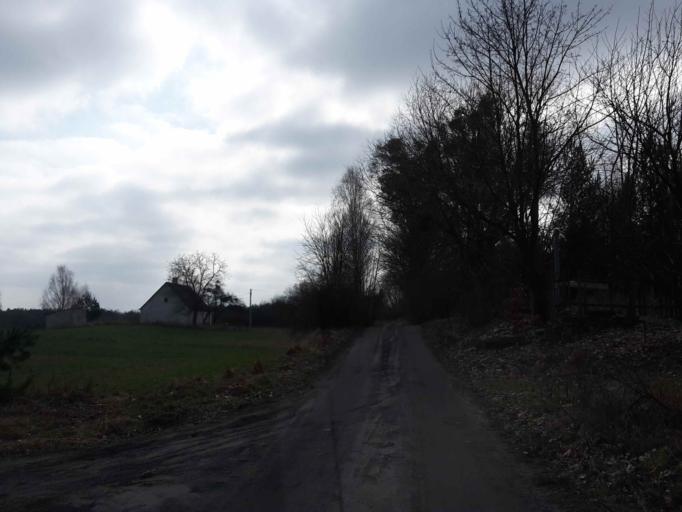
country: PL
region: Kujawsko-Pomorskie
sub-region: Powiat brodnicki
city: Brodnica
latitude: 53.3161
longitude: 19.3575
